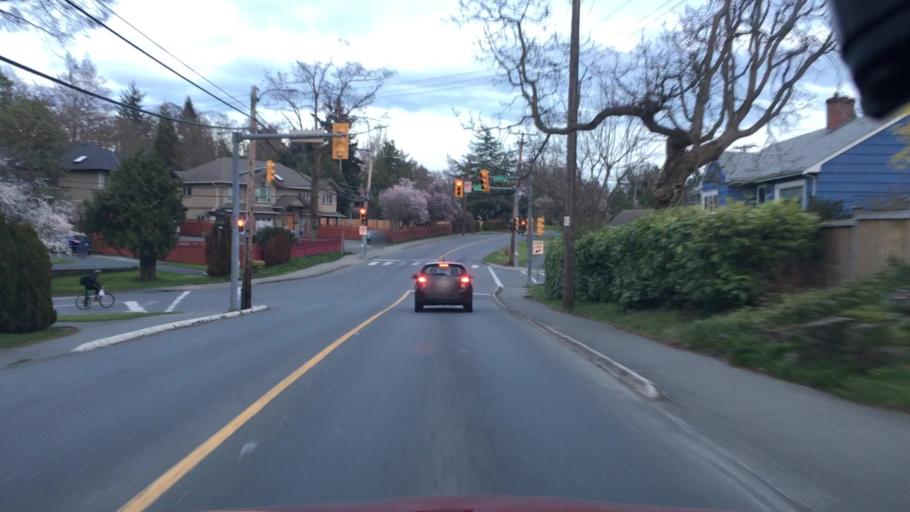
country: CA
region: British Columbia
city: Victoria
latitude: 48.4653
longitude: -123.3452
